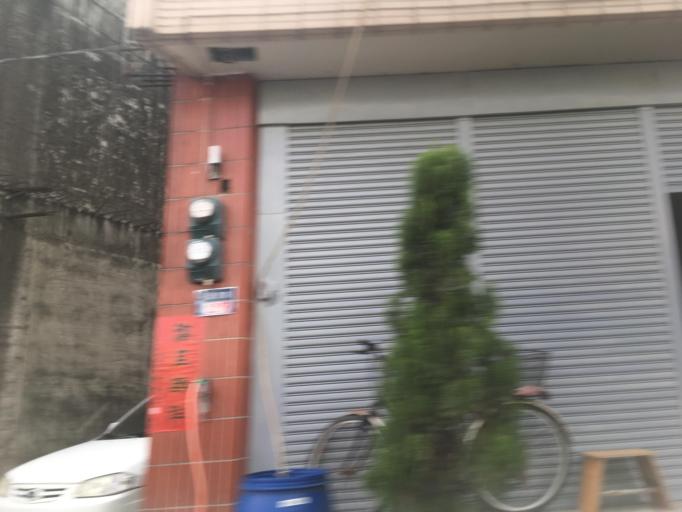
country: TW
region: Taiwan
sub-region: Yunlin
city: Douliu
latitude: 23.6898
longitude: 120.4674
